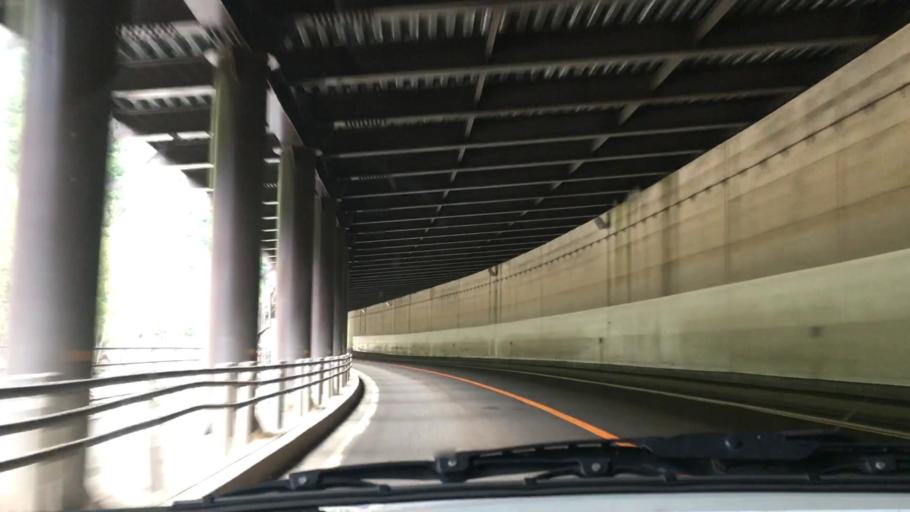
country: JP
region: Hokkaido
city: Otofuke
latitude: 43.3617
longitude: 143.2398
